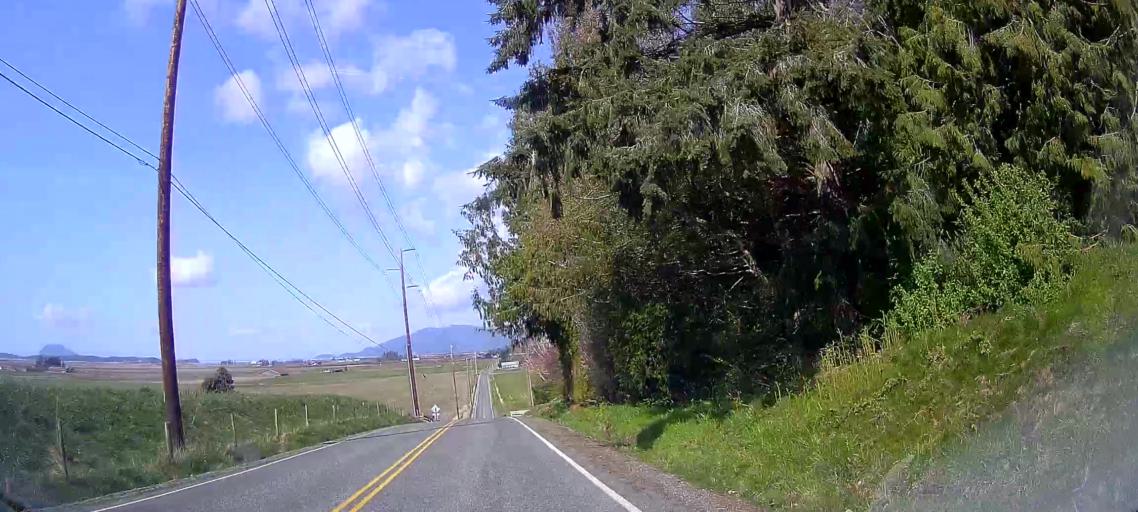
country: US
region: Washington
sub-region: Skagit County
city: Burlington
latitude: 48.5101
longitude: -122.4443
